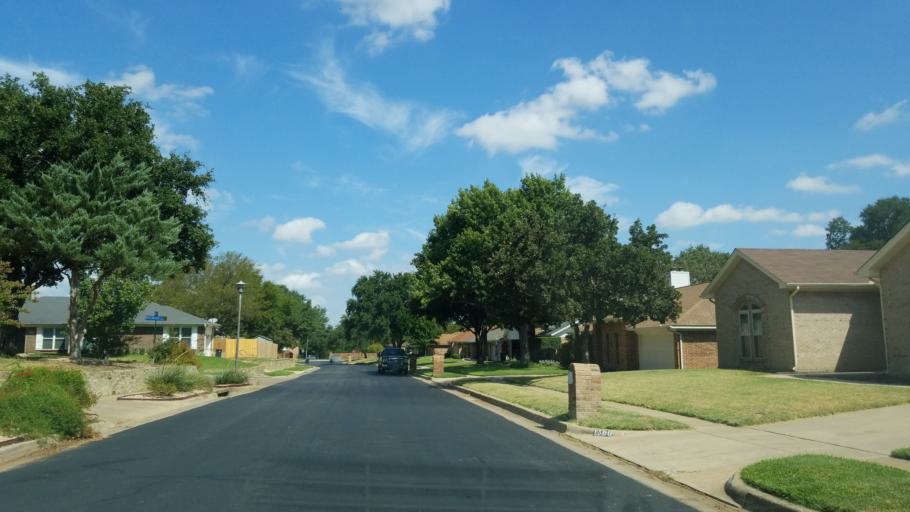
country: US
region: Texas
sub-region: Tarrant County
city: Euless
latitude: 32.8574
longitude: -97.0969
